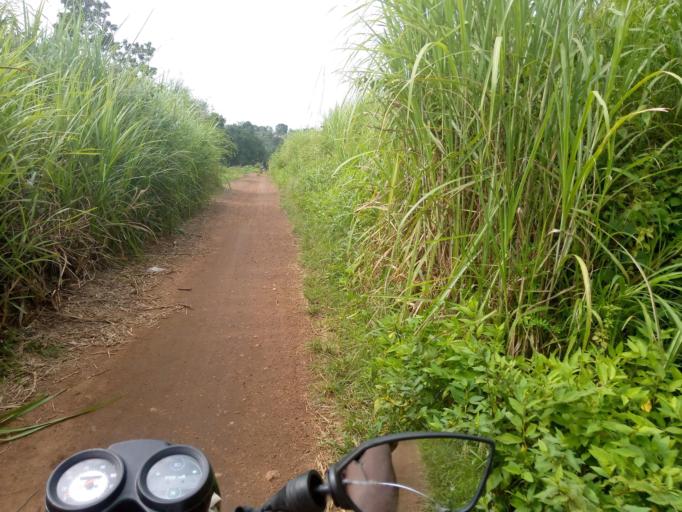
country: SL
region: Eastern Province
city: Buedu
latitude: 8.4540
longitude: -10.3345
